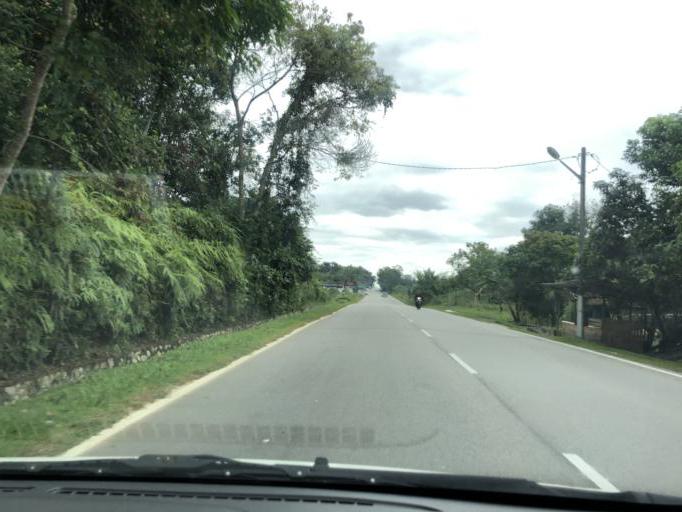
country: MY
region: Putrajaya
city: Putrajaya
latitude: 2.9284
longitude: 101.7472
